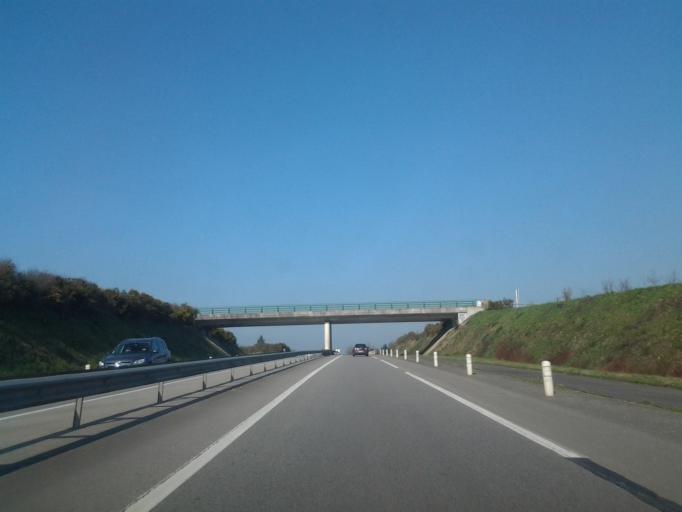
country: FR
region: Pays de la Loire
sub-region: Departement de la Vendee
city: Mache
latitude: 46.7718
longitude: -1.6694
